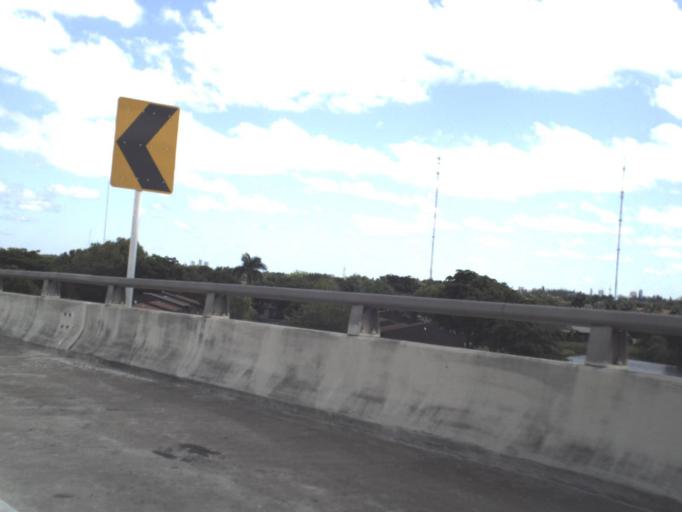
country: US
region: Florida
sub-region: Broward County
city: Miramar
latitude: 25.9734
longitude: -80.2297
